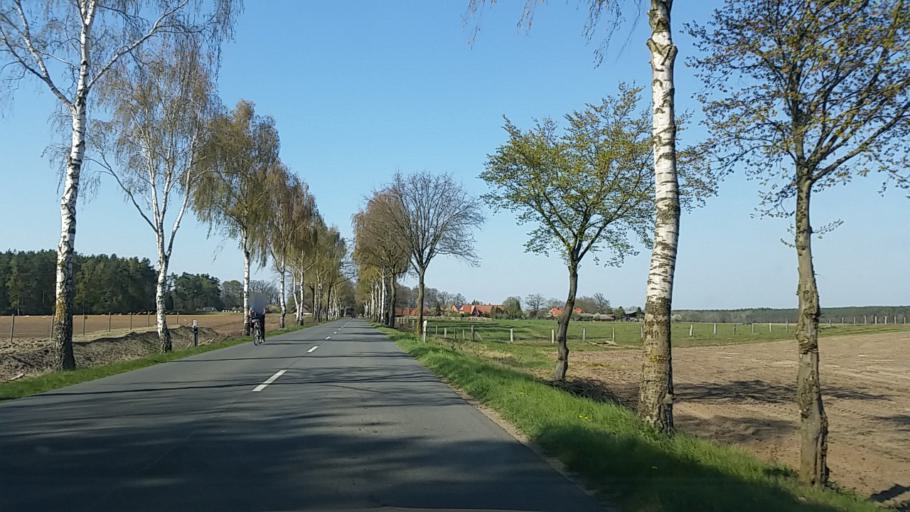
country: DE
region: Lower Saxony
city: Rullstorf
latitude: 53.2630
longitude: 10.5201
